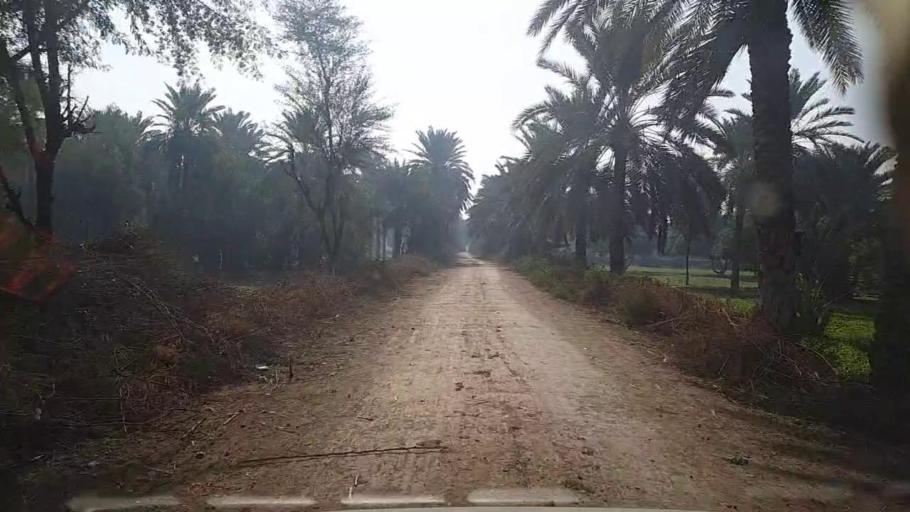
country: PK
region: Sindh
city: Kandiari
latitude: 26.9729
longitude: 68.4694
